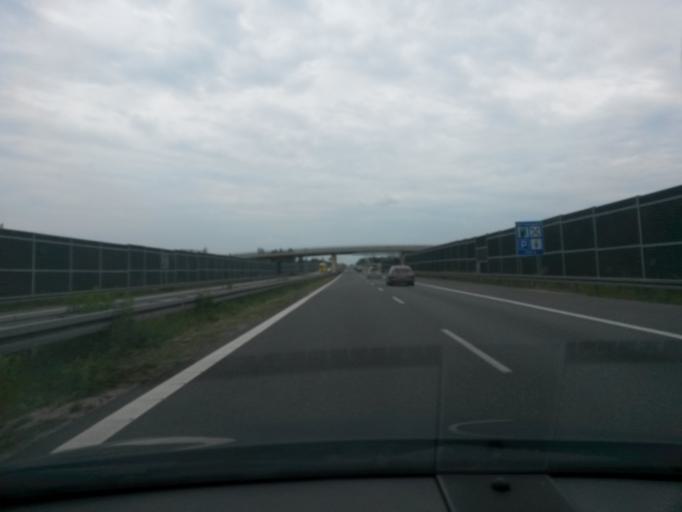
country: PL
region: Masovian Voivodeship
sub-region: Powiat zyrardowski
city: Radziejowice
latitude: 51.9975
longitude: 20.5523
